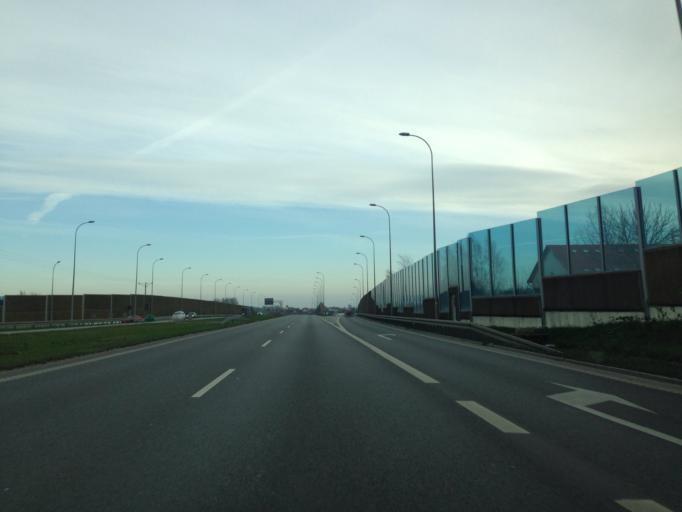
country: PL
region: Pomeranian Voivodeship
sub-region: Powiat gdanski
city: Kowale
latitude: 54.3473
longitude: 18.5328
